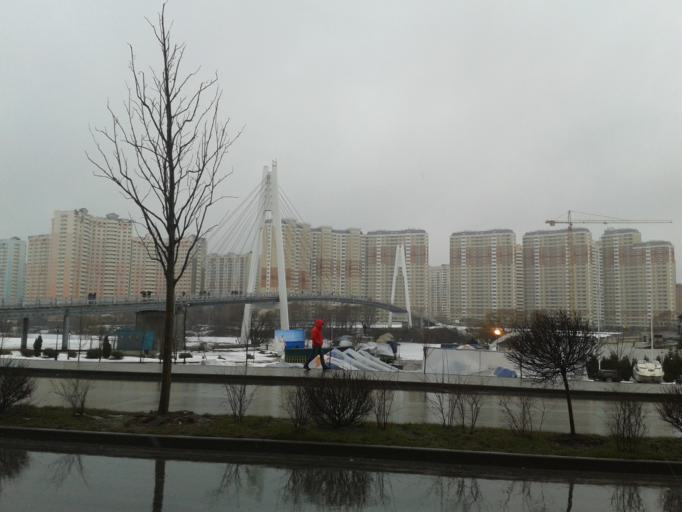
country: RU
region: Moscow
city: Strogino
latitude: 55.8208
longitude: 37.3854
